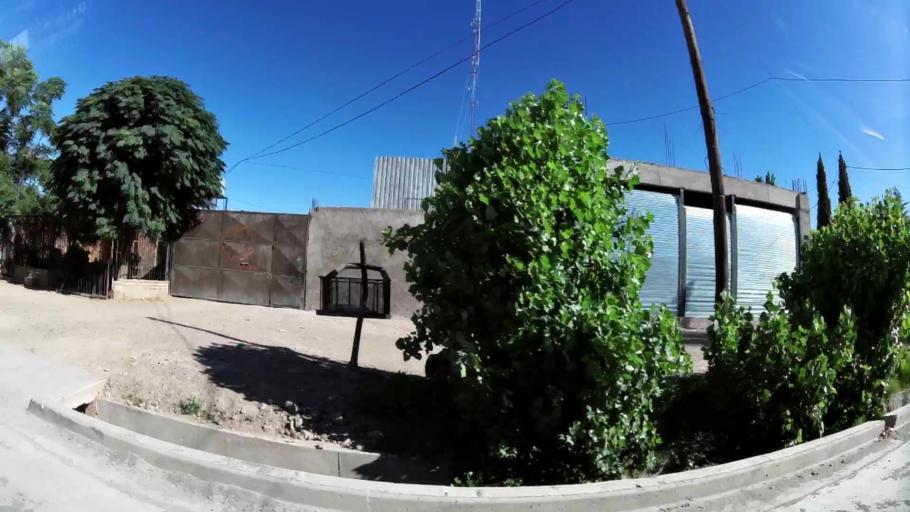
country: AR
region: Mendoza
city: Las Heras
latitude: -32.8325
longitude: -68.8278
